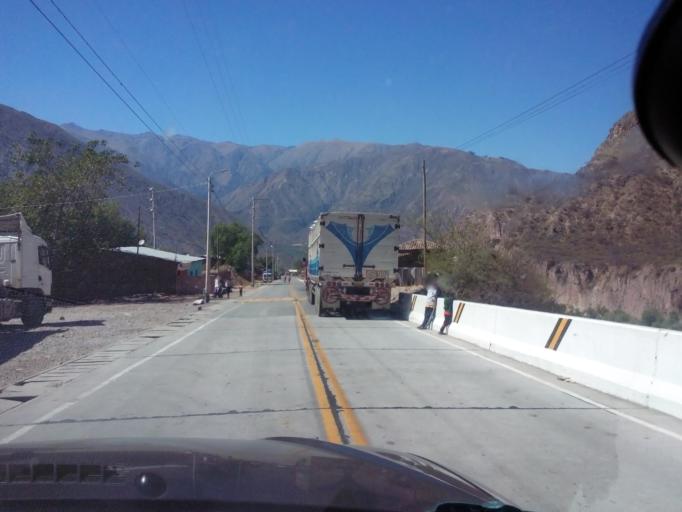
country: PE
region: Ayacucho
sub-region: Provincia de Huamanga
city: Ocros
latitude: -13.4224
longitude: -73.8553
